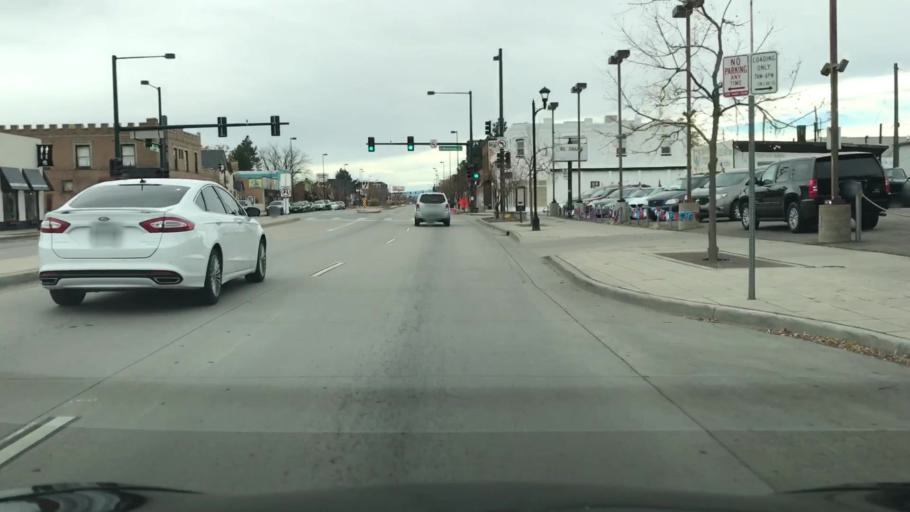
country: US
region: Colorado
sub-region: Arapahoe County
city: Englewood
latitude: 39.6917
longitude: -104.9876
